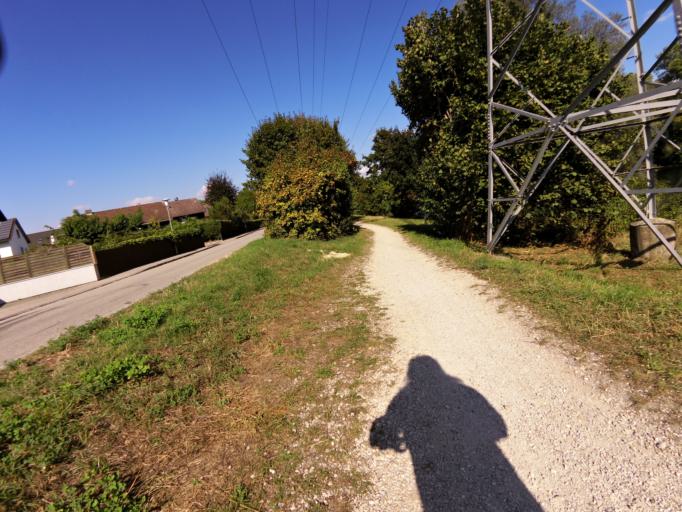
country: DE
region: Bavaria
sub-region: Lower Bavaria
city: Ergolding
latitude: 48.5525
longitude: 12.1706
